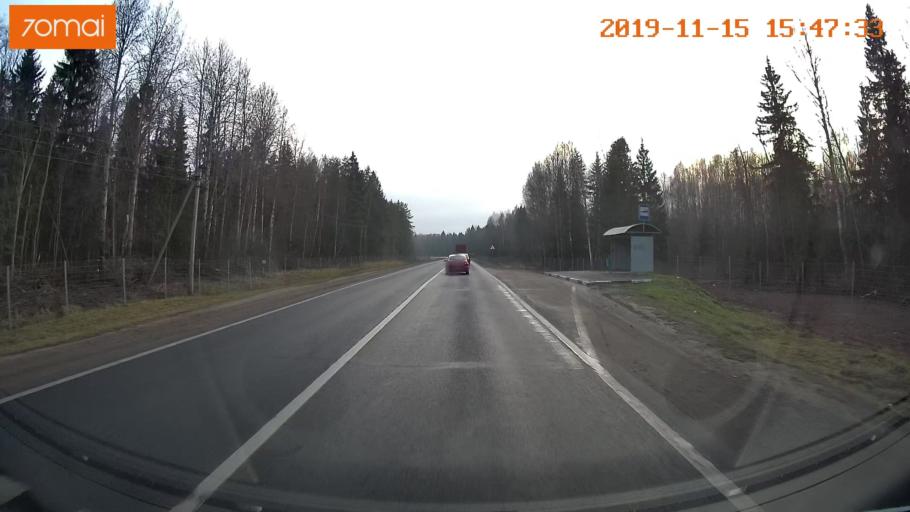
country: RU
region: Jaroslavl
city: Danilov
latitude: 57.9370
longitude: 40.0089
